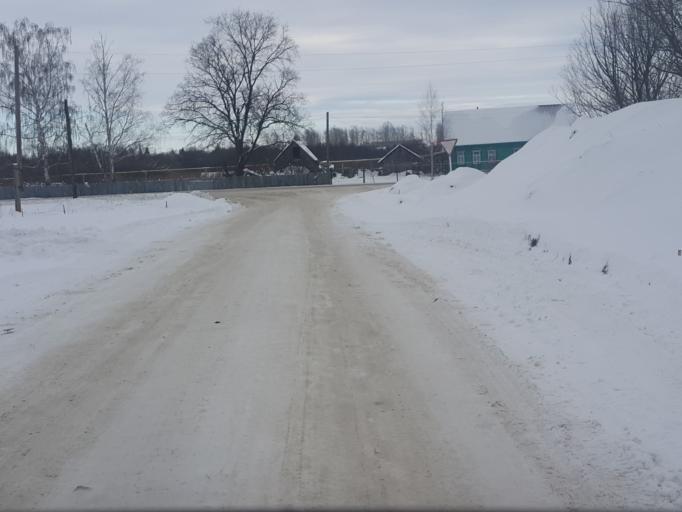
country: RU
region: Tambov
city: Platonovka
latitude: 52.8803
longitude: 41.8762
